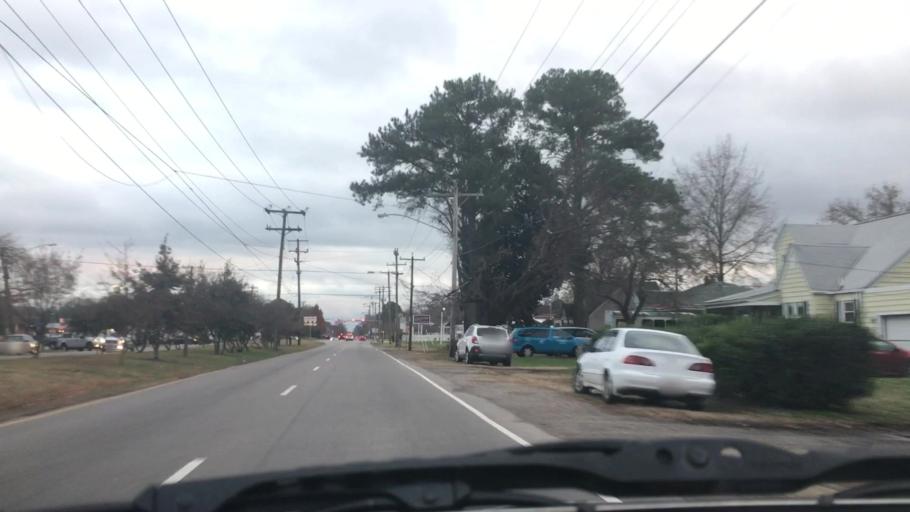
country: US
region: Virginia
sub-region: City of Norfolk
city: Norfolk
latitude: 36.9174
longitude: -76.2421
